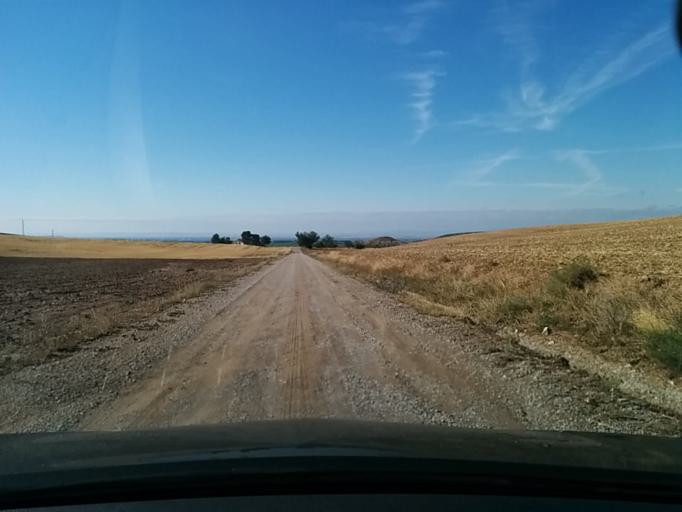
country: ES
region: Aragon
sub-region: Provincia de Zaragoza
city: Tauste
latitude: 42.0163
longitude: -1.3043
